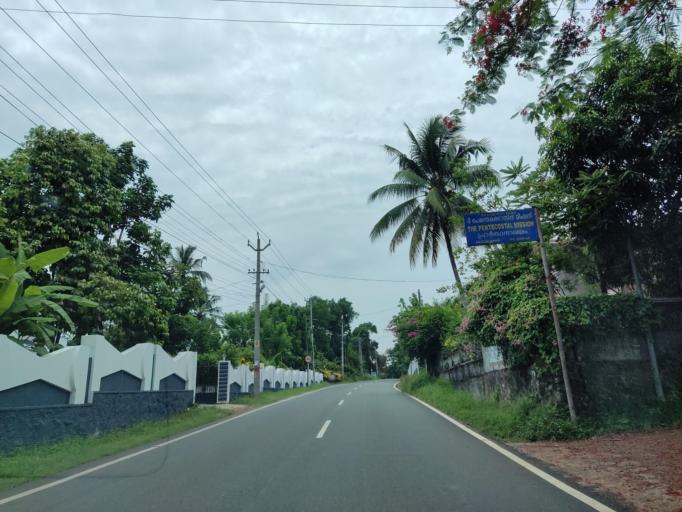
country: IN
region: Kerala
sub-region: Alappuzha
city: Chengannur
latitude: 9.2740
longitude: 76.6139
